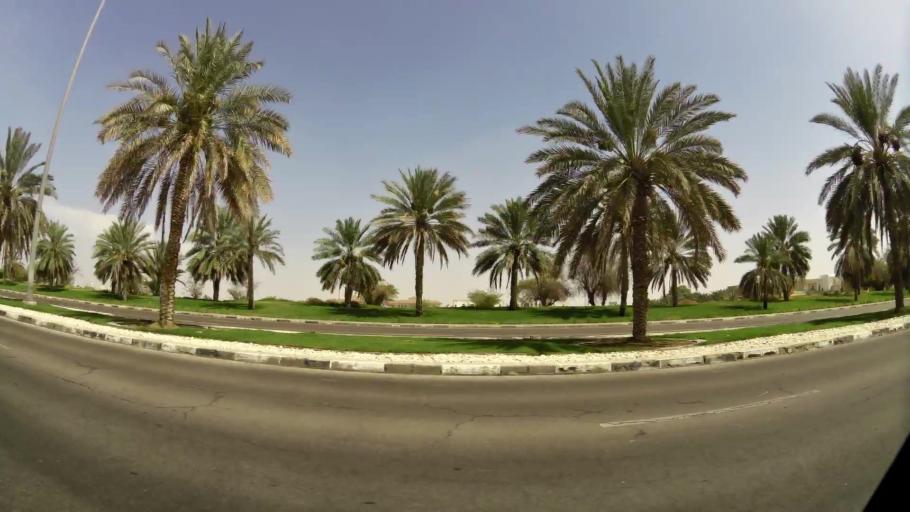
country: AE
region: Abu Dhabi
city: Al Ain
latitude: 24.2245
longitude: 55.7042
